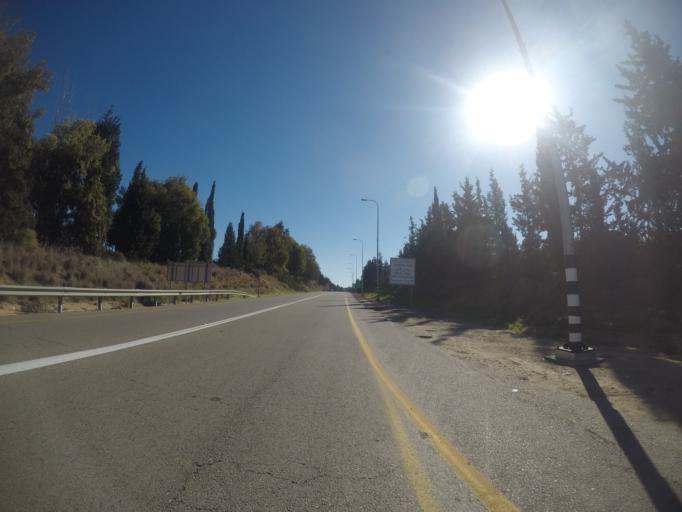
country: IL
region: Southern District
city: Ashdod
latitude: 31.7239
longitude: 34.6365
